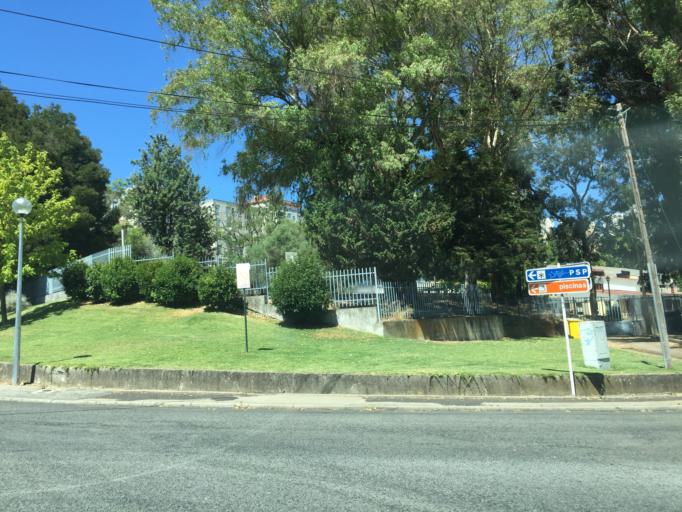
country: PT
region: Lisbon
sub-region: Odivelas
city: Povoa de Santo Adriao
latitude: 38.8118
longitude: -9.1625
